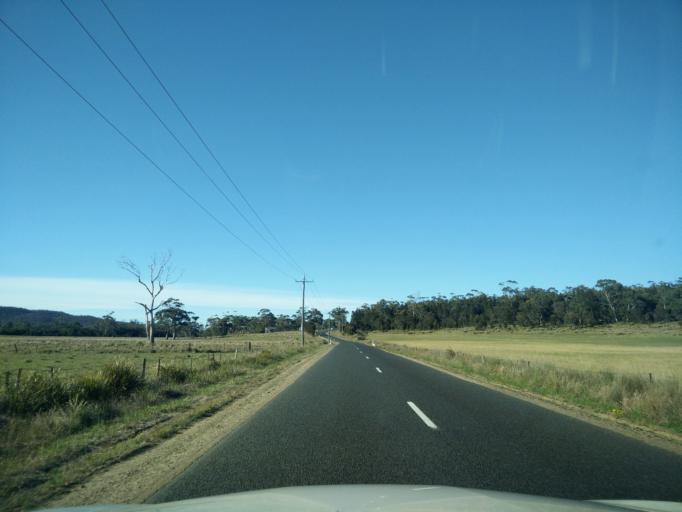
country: AU
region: Tasmania
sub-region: Break O'Day
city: St Helens
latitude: -41.9128
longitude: 148.2501
